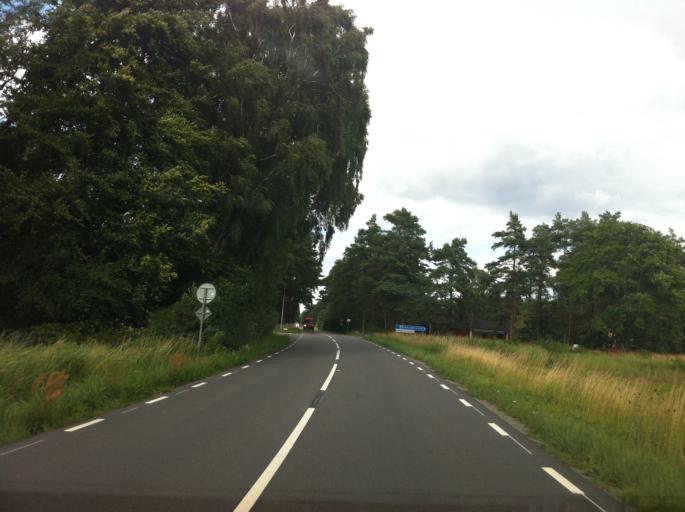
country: SE
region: Skane
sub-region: Simrishamns Kommun
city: Simrishamn
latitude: 55.4048
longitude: 14.1865
